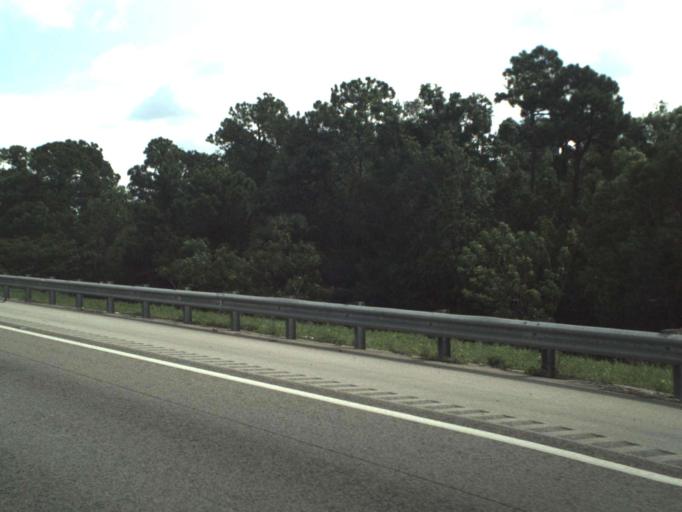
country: US
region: Florida
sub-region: Palm Beach County
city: Limestone Creek
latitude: 26.9283
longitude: -80.1482
